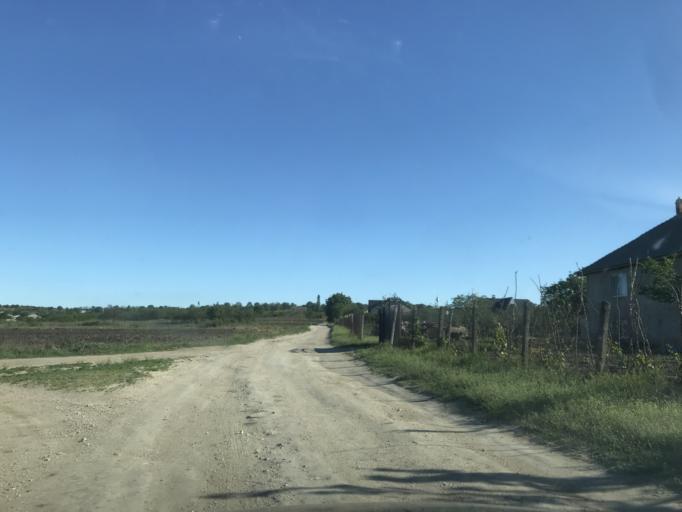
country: MD
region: Chisinau
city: Cricova
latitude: 47.2348
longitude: 28.8155
